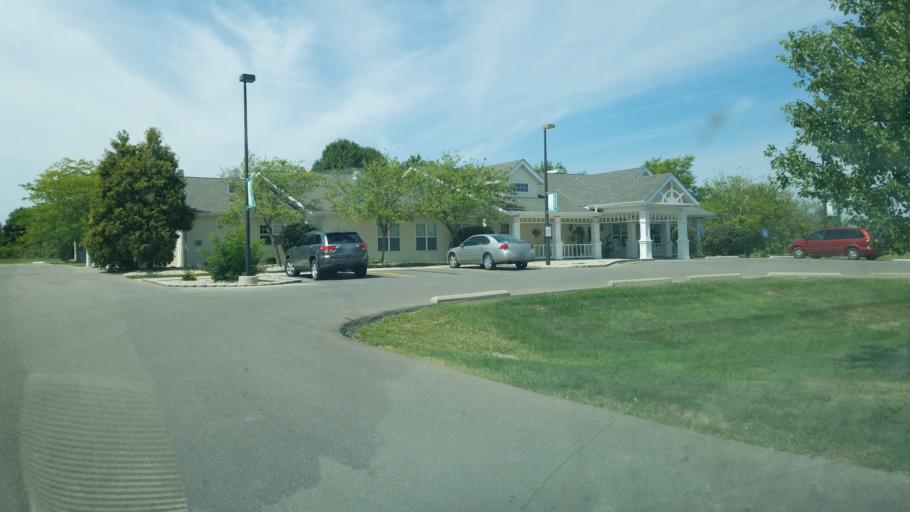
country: US
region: Ohio
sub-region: Hardin County
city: Kenton
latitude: 40.6558
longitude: -83.5935
